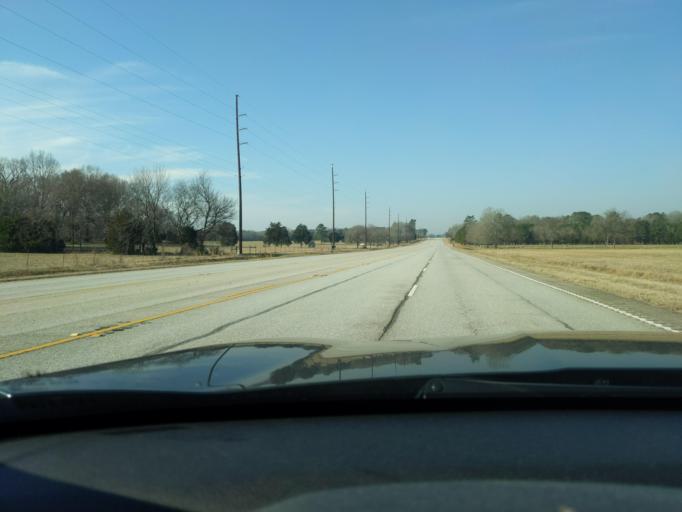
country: US
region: South Carolina
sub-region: Abbeville County
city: Calhoun Falls
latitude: 34.1009
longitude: -82.5476
